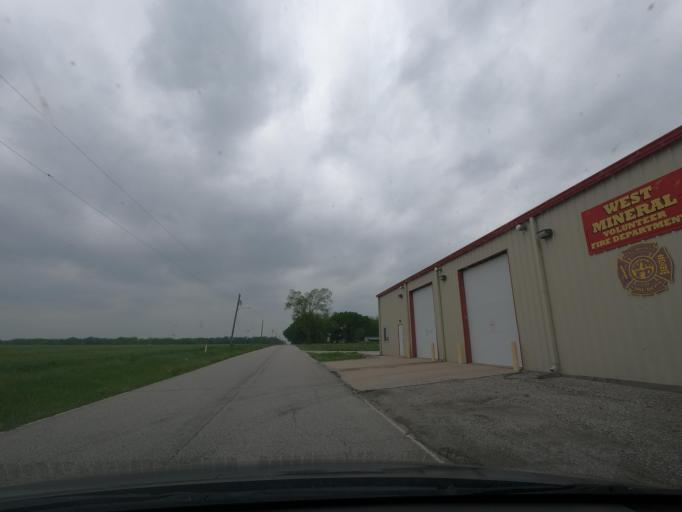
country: US
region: Kansas
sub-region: Cherokee County
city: Columbus
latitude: 37.2817
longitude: -94.9251
